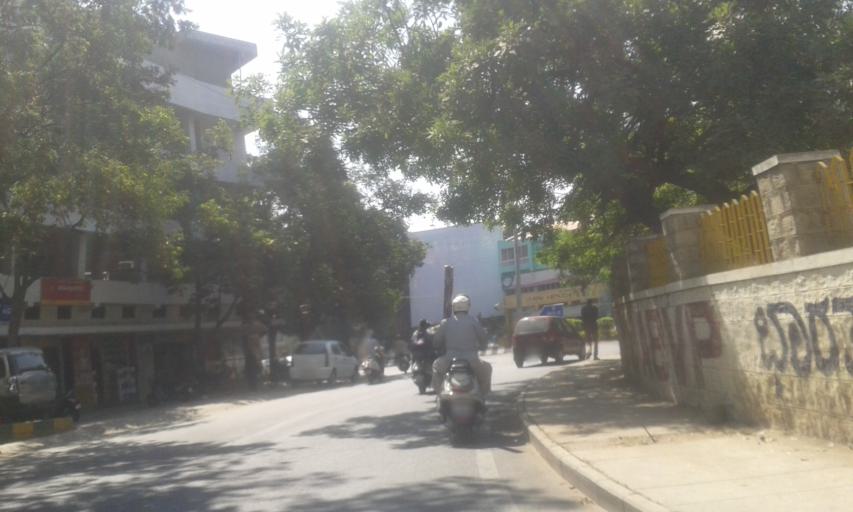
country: IN
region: Karnataka
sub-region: Bangalore Urban
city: Bangalore
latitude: 12.9402
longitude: 77.5777
